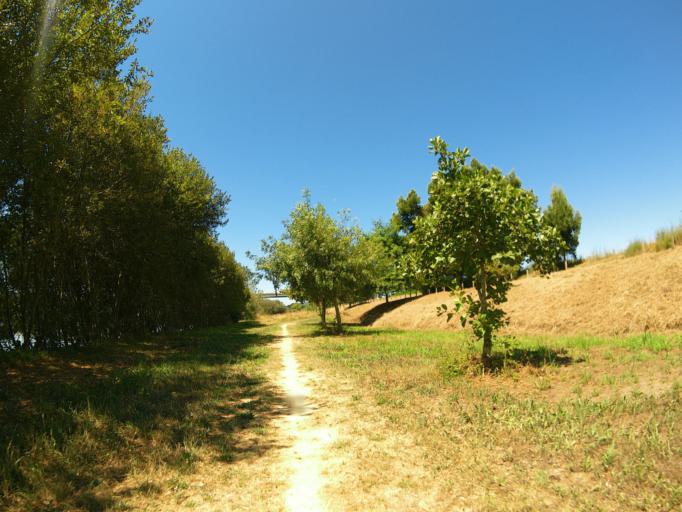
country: PT
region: Viana do Castelo
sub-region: Viana do Castelo
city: Darque
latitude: 41.7262
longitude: -8.6812
